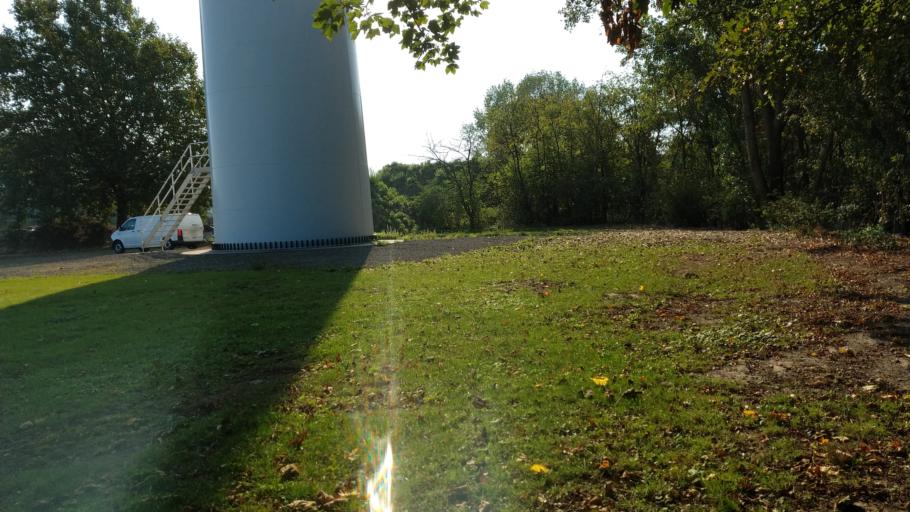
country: BE
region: Flanders
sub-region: Provincie Oost-Vlaanderen
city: Zelzate
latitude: 51.1868
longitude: 3.8280
